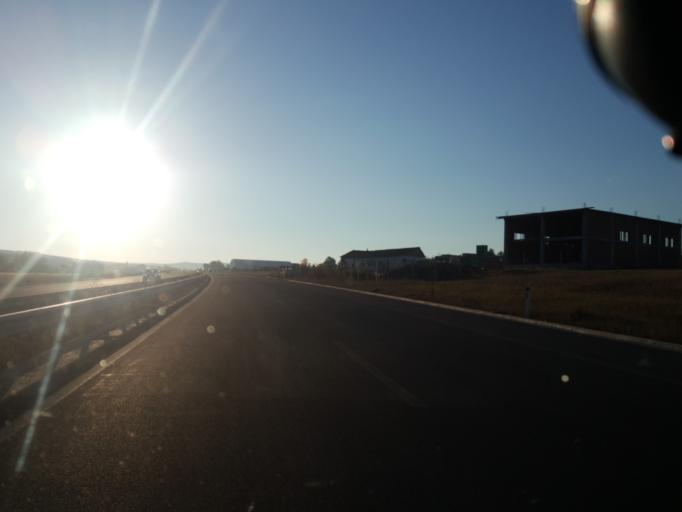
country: XK
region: Prizren
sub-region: Komuna e Malisheves
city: Llazice
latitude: 42.5691
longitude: 20.7380
